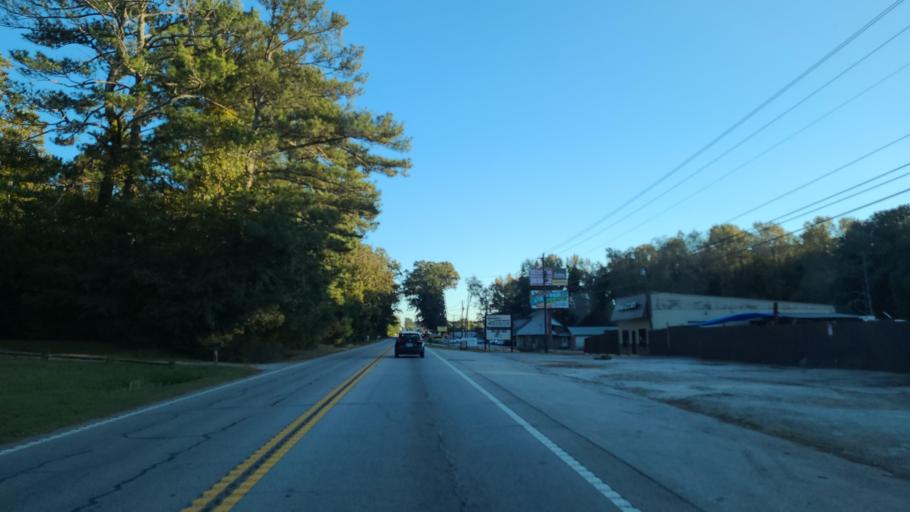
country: US
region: Georgia
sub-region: Henry County
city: Stockbridge
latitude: 33.5598
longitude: -84.2605
